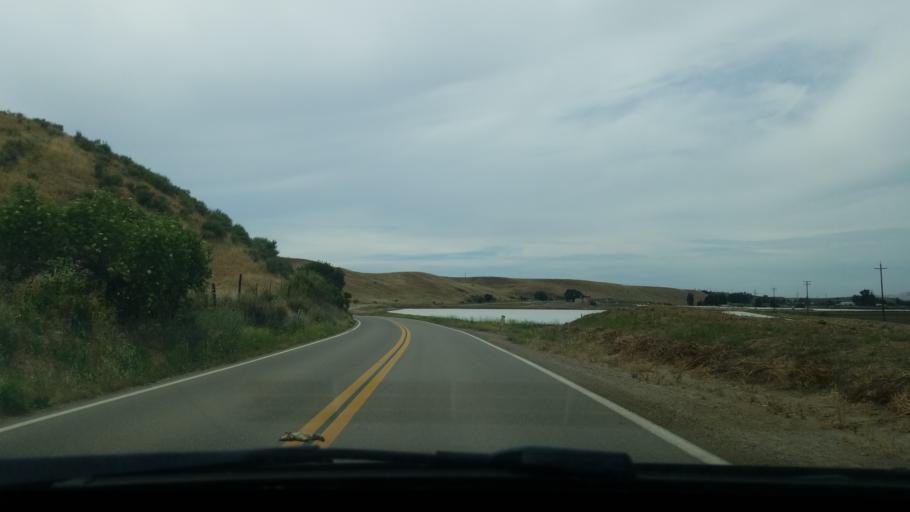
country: US
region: California
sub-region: Santa Barbara County
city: Los Alamos
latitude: 34.8726
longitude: -120.3043
